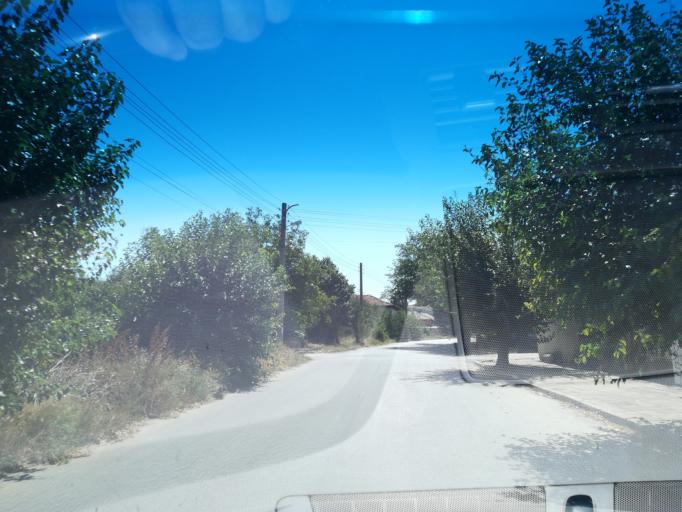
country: BG
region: Pazardzhik
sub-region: Obshtina Pazardzhik
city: Pazardzhik
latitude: 42.3377
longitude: 24.4015
